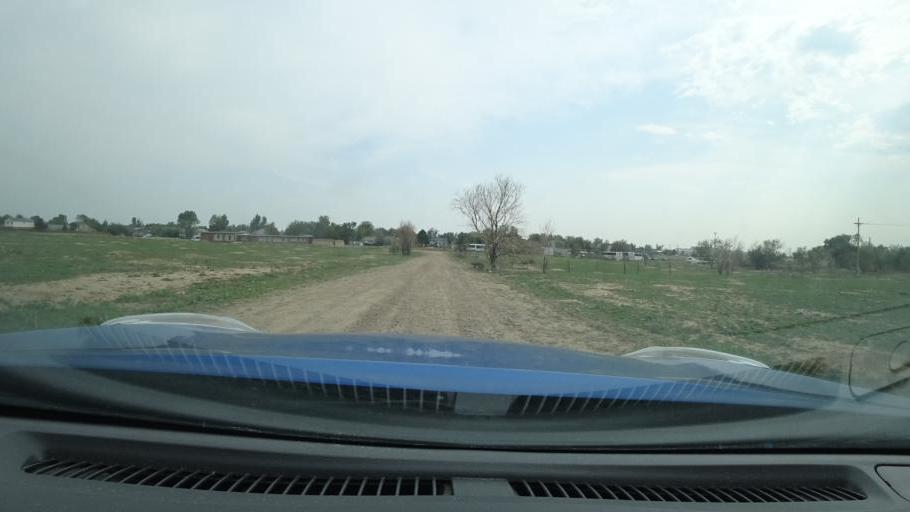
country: US
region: Colorado
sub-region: Adams County
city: Aurora
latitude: 39.7524
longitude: -104.7691
